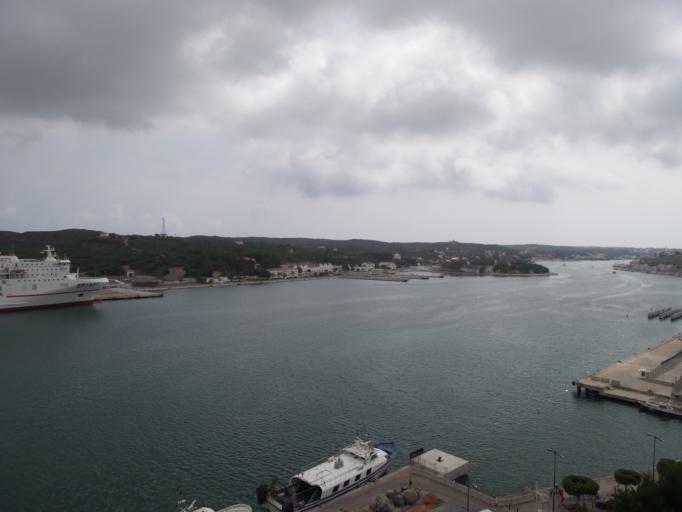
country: ES
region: Balearic Islands
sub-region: Illes Balears
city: Mao
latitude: 39.8914
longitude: 4.2610
